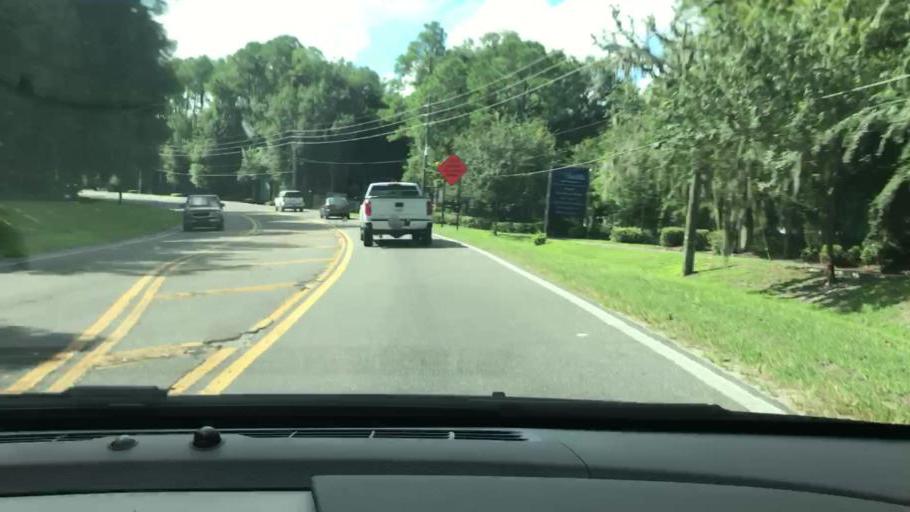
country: US
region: Florida
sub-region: Alachua County
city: Gainesville
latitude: 29.6515
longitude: -82.4089
